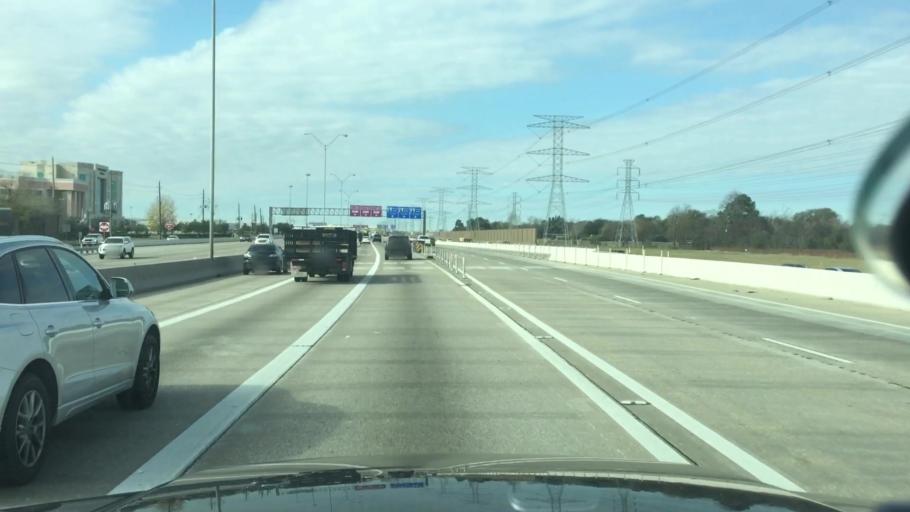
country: US
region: Texas
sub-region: Harris County
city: Hudson
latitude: 29.9378
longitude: -95.4644
